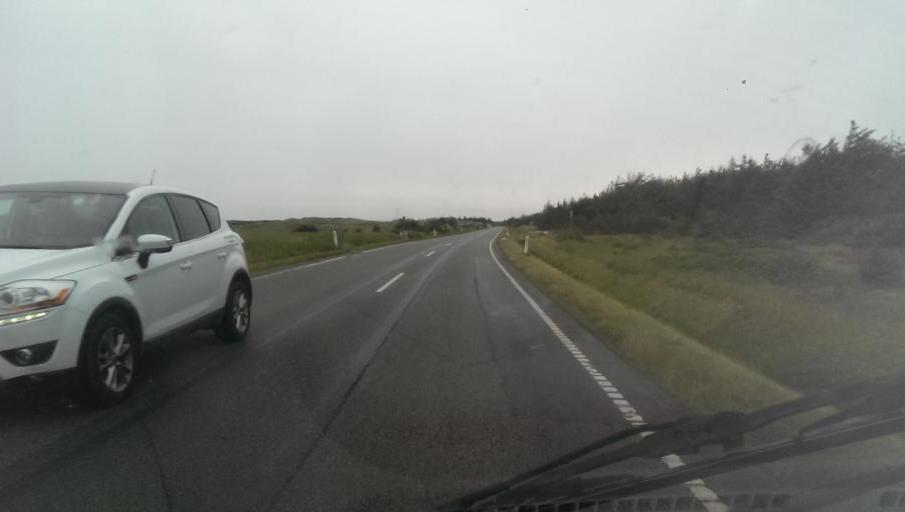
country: DK
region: Central Jutland
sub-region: Ringkobing-Skjern Kommune
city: Hvide Sande
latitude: 55.9367
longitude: 8.1580
